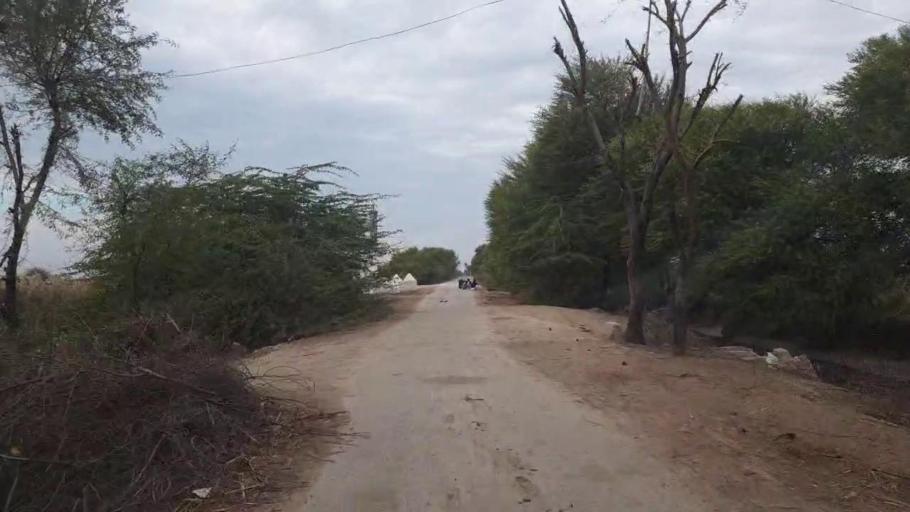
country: PK
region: Sindh
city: Jhol
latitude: 25.9956
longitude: 68.8907
